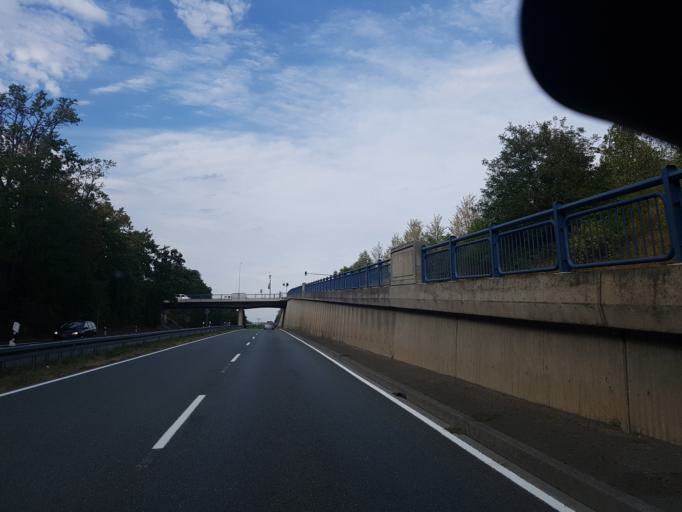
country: DE
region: Saxony
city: Riesa
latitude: 51.3028
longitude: 13.2846
